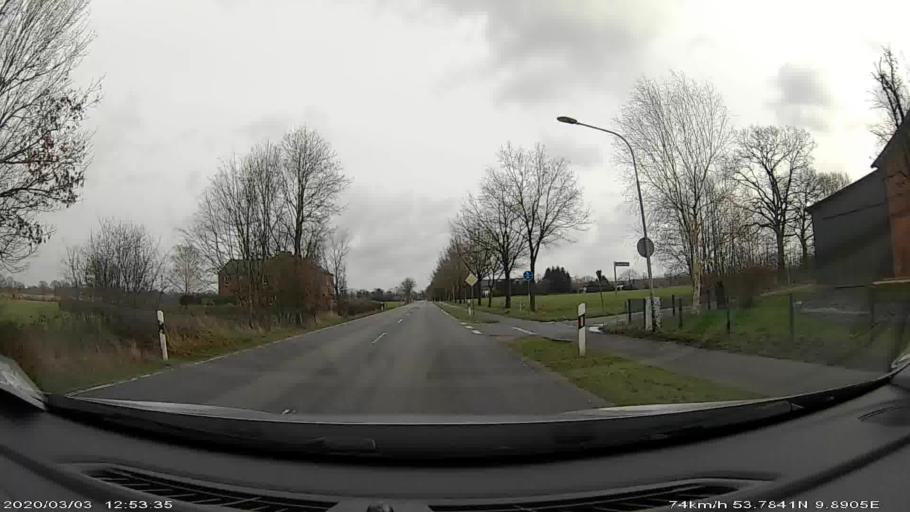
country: DE
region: Schleswig-Holstein
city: Bilsen
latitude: 53.7840
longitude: 9.8937
